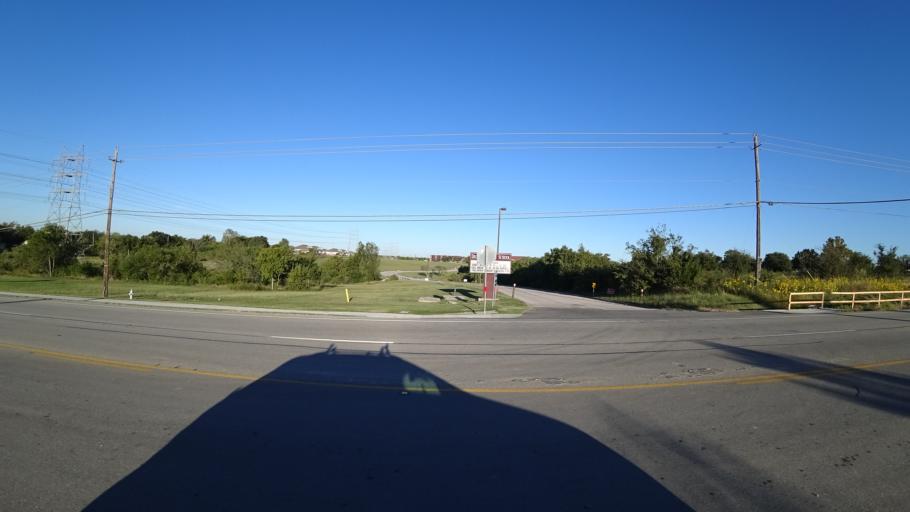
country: US
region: Texas
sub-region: Travis County
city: Manor
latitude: 30.3082
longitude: -97.6170
